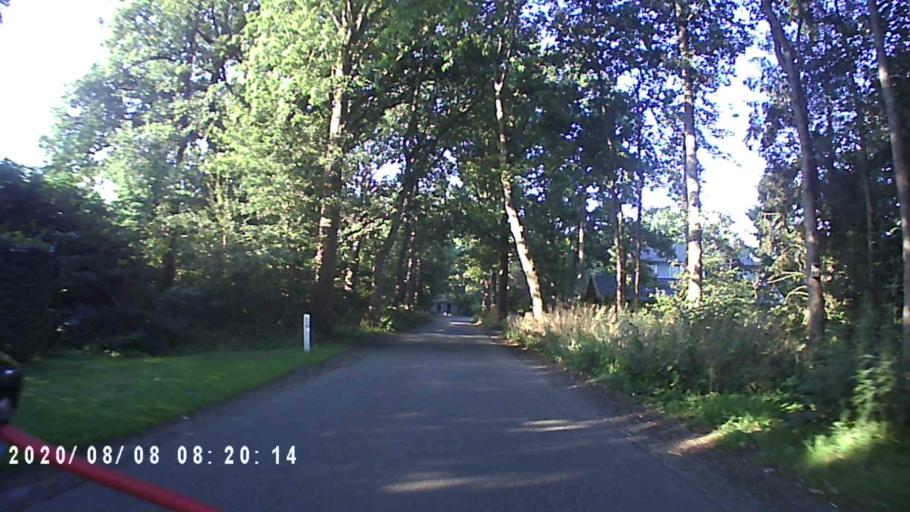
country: NL
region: Groningen
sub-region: Gemeente Leek
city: Leek
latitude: 53.0940
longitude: 6.3144
